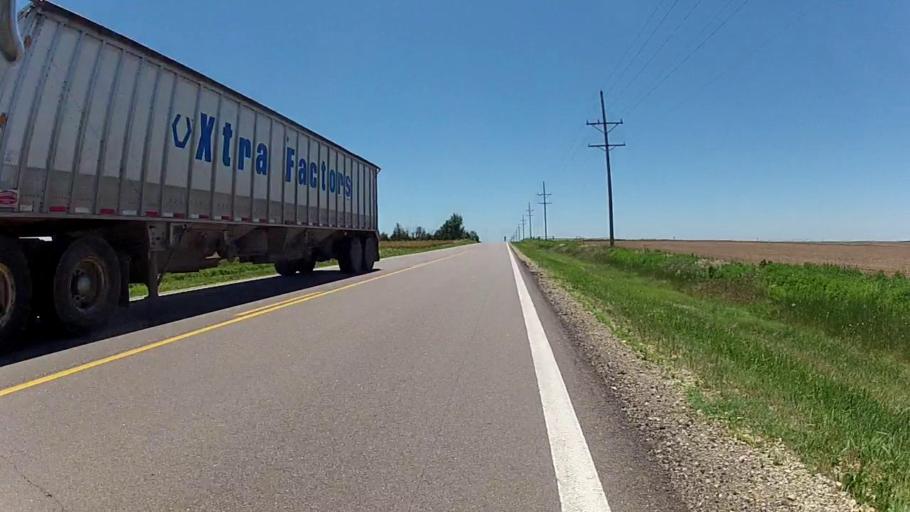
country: US
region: Kansas
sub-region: Kiowa County
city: Greensburg
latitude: 37.5215
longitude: -99.3206
